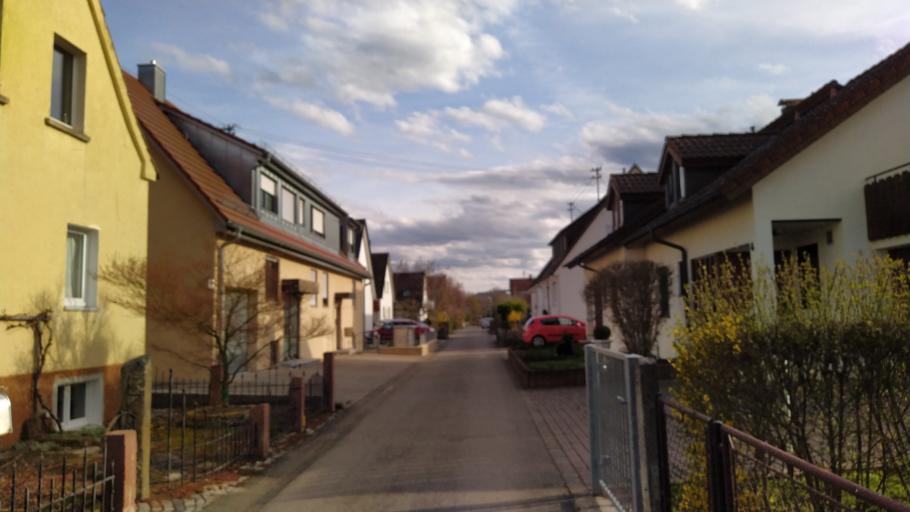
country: DE
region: Baden-Wuerttemberg
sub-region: Tuebingen Region
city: Rottenburg
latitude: 48.5009
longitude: 8.9915
